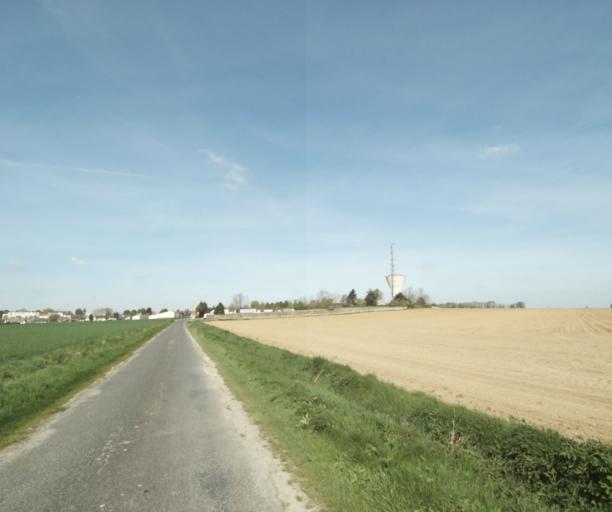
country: FR
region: Ile-de-France
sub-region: Departement de Seine-et-Marne
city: Nangis
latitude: 48.5521
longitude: 3.0292
